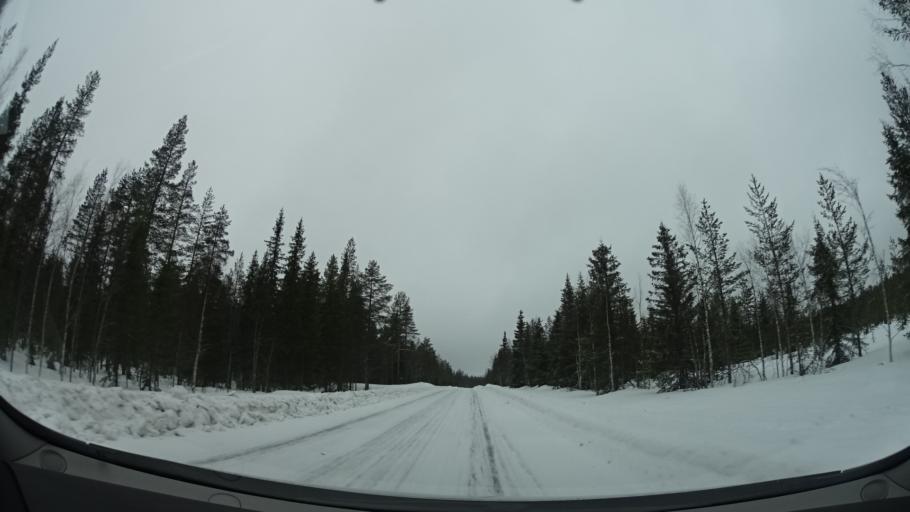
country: SE
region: Vaesterbotten
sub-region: Mala Kommun
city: Mala
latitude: 65.0986
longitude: 18.9126
